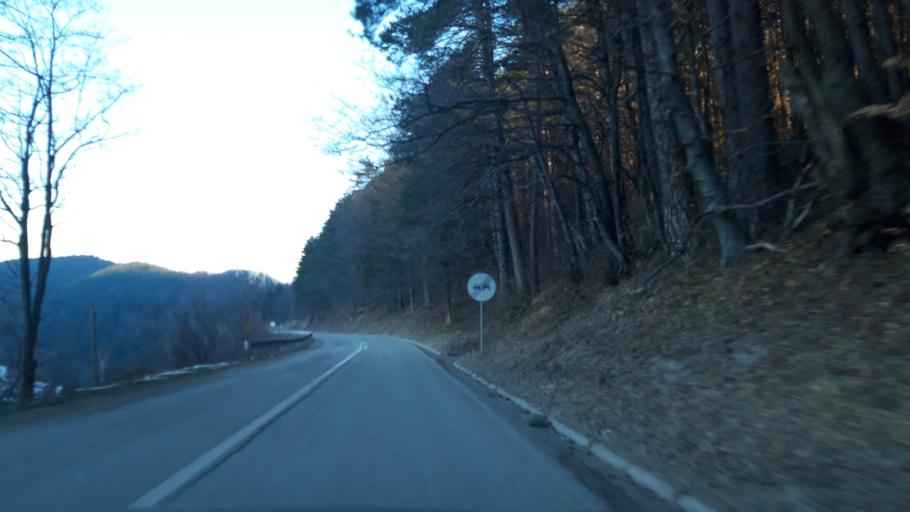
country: BA
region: Republika Srpska
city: Vlasenica
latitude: 44.1686
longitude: 18.9495
